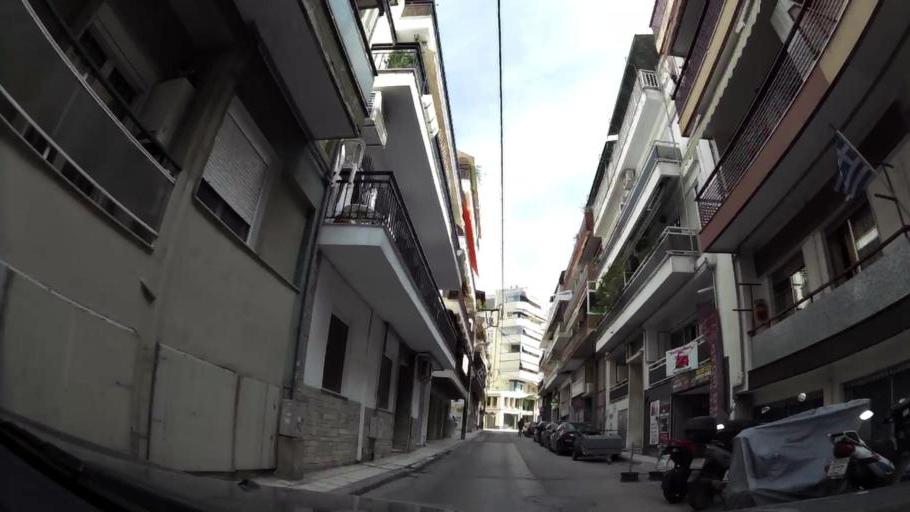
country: GR
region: Central Macedonia
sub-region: Nomos Thessalonikis
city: Kalamaria
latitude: 40.5875
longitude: 22.9652
